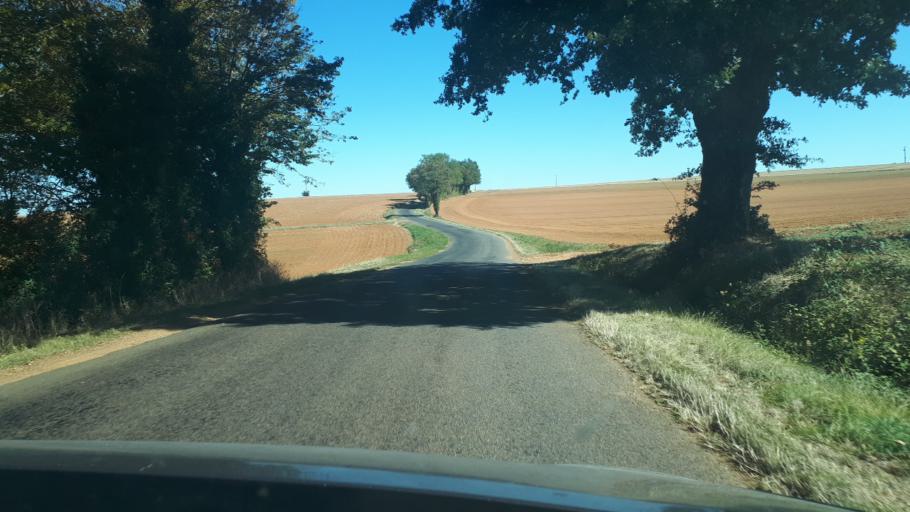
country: FR
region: Centre
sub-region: Departement du Cher
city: Sancerre
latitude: 47.3211
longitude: 2.7714
